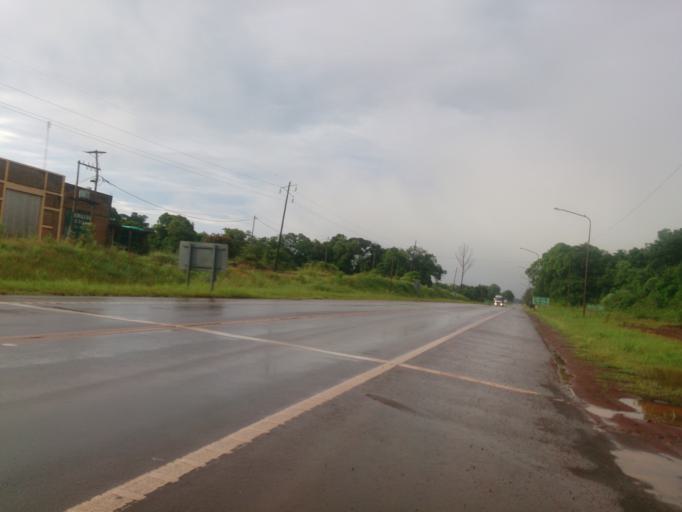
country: AR
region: Misiones
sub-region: Departamento de Obera
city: Obera
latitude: -27.4732
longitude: -55.0862
